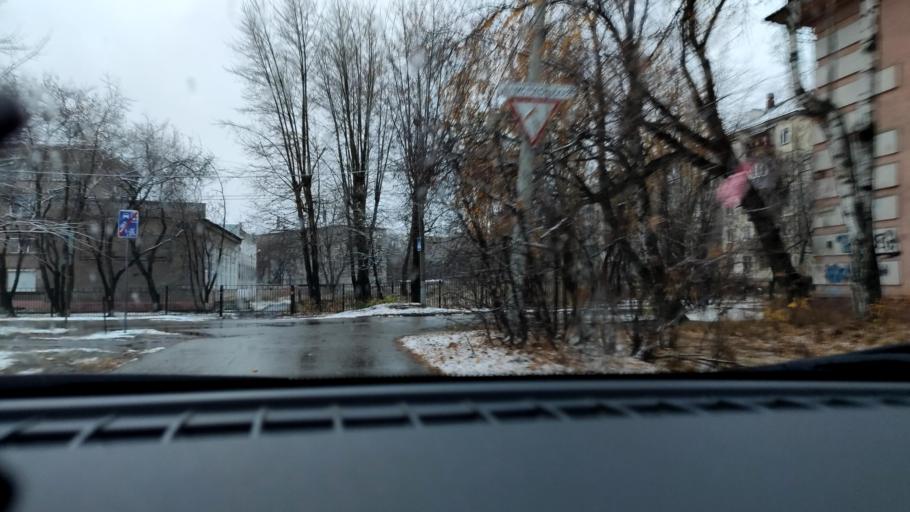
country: RU
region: Perm
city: Kultayevo
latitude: 57.9961
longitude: 55.9407
